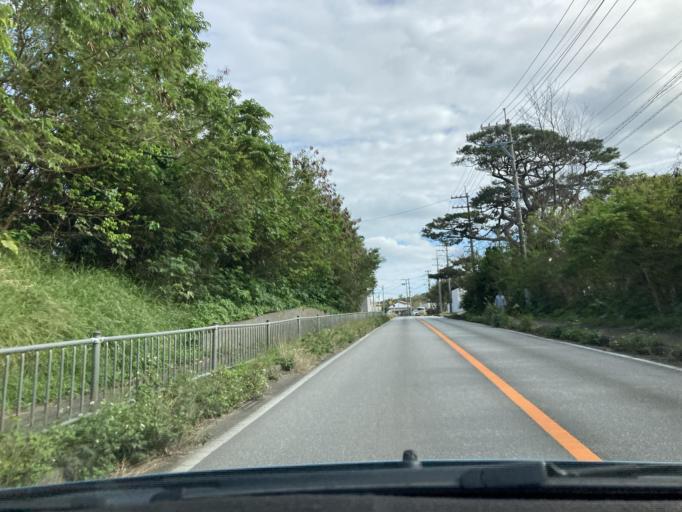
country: JP
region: Okinawa
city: Nago
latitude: 26.6987
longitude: 127.9332
